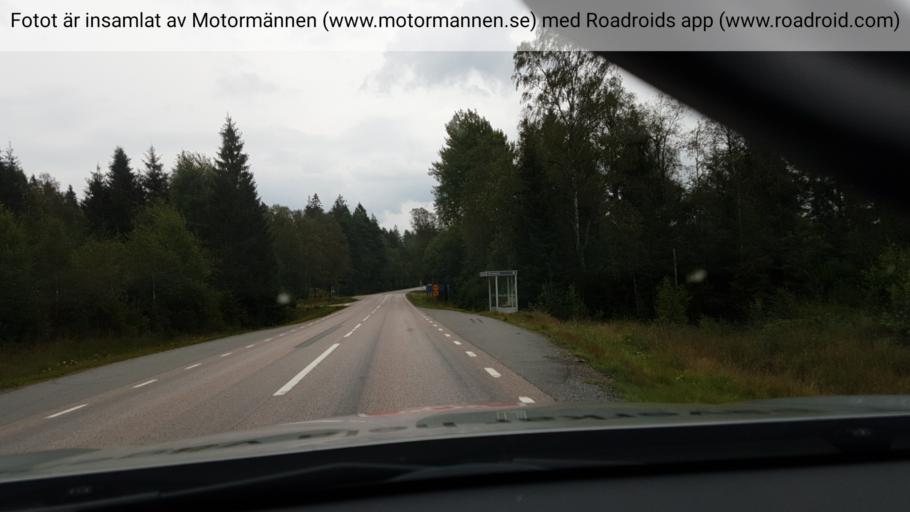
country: SE
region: Vaestra Goetaland
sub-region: Svenljunga Kommun
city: Svenljunga
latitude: 57.4883
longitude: 12.9945
